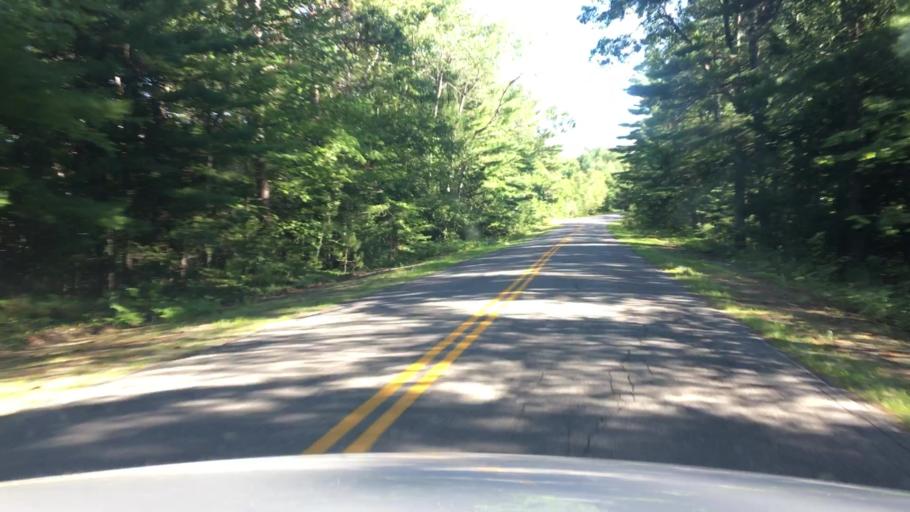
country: US
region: Maine
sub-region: Penobscot County
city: Enfield
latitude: 45.2278
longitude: -68.5801
